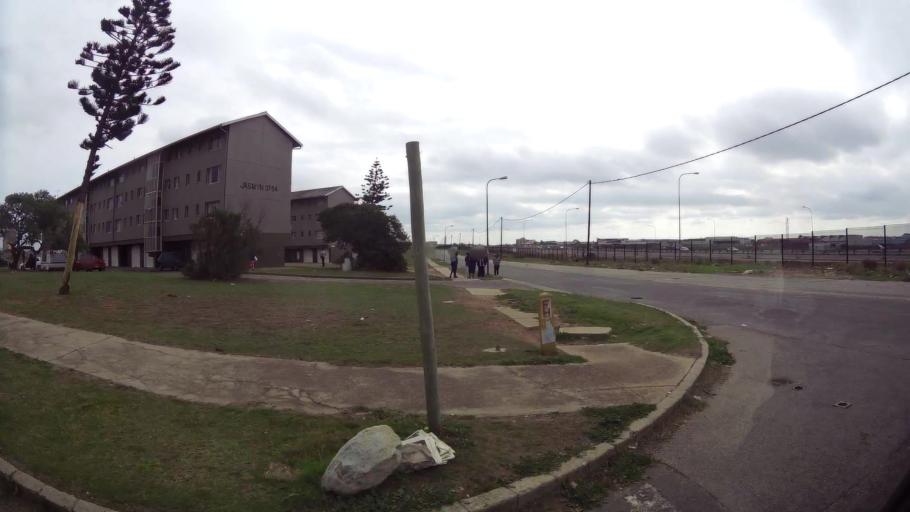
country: ZA
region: Eastern Cape
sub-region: Nelson Mandela Bay Metropolitan Municipality
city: Port Elizabeth
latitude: -33.8911
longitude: 25.5632
